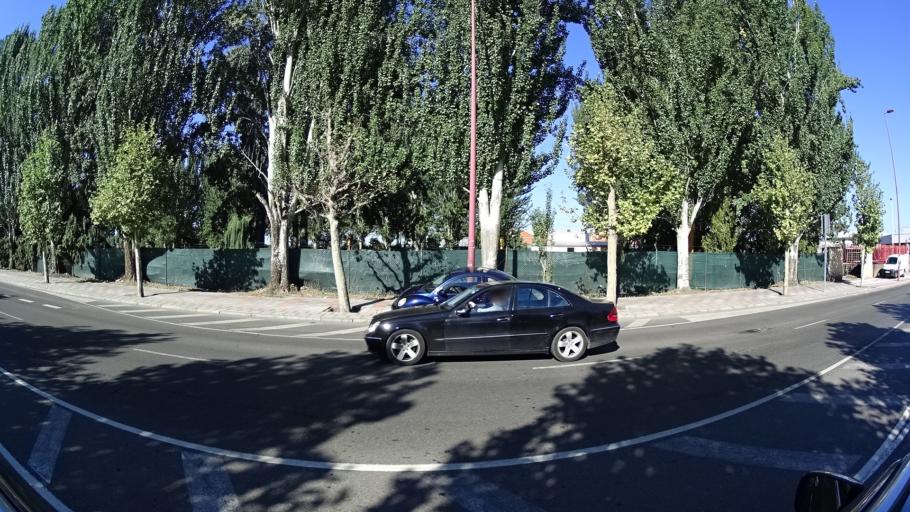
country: ES
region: Castille and Leon
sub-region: Provincia de Leon
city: Leon
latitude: 42.5915
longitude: -5.5777
